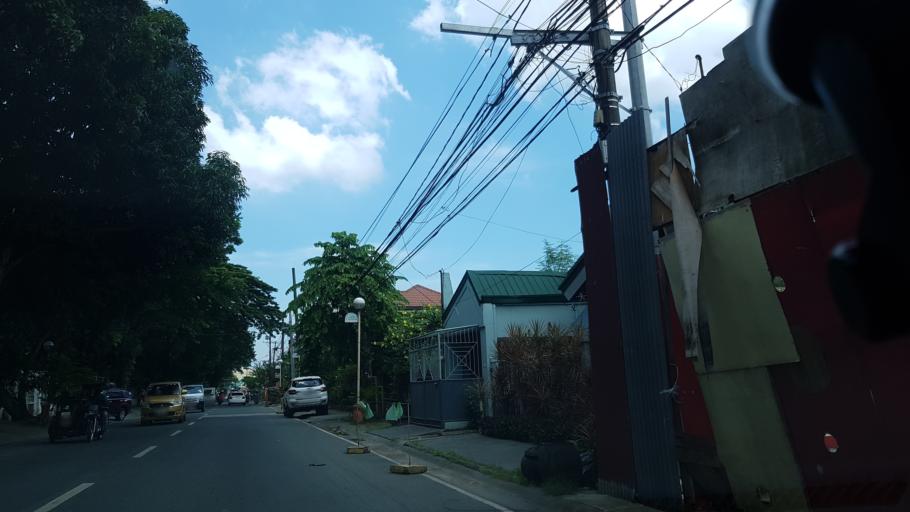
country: PH
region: Calabarzon
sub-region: Province of Rizal
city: Las Pinas
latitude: 14.4330
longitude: 120.9853
